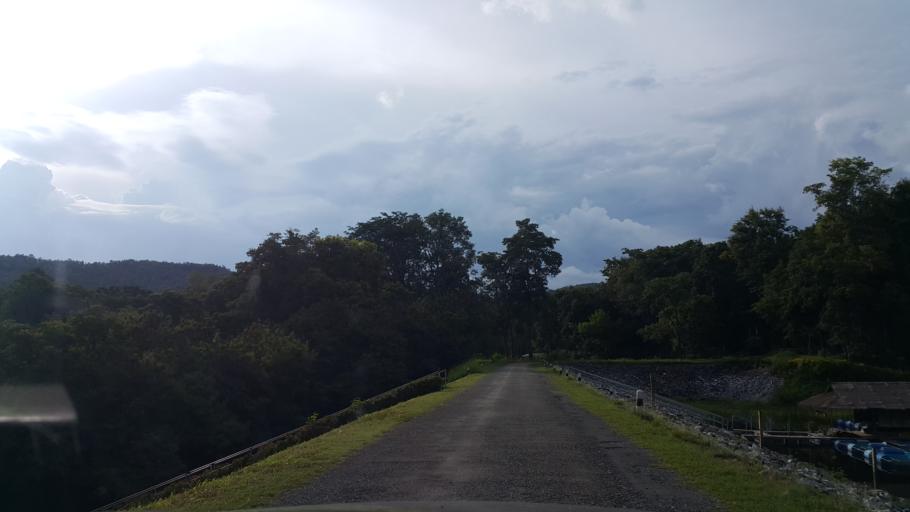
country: TH
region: Chiang Mai
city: Mae On
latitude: 18.8786
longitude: 99.2173
